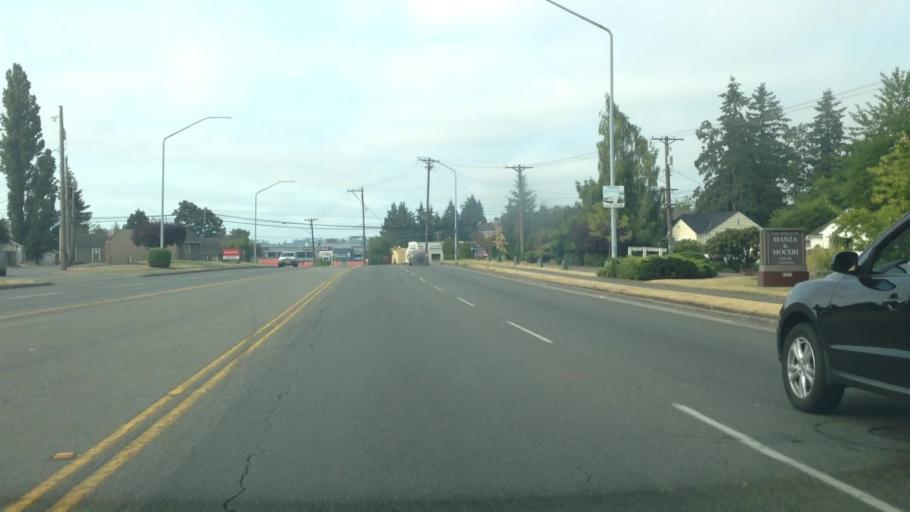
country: US
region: Washington
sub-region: Pierce County
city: Fircrest
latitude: 47.2335
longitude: -122.4831
